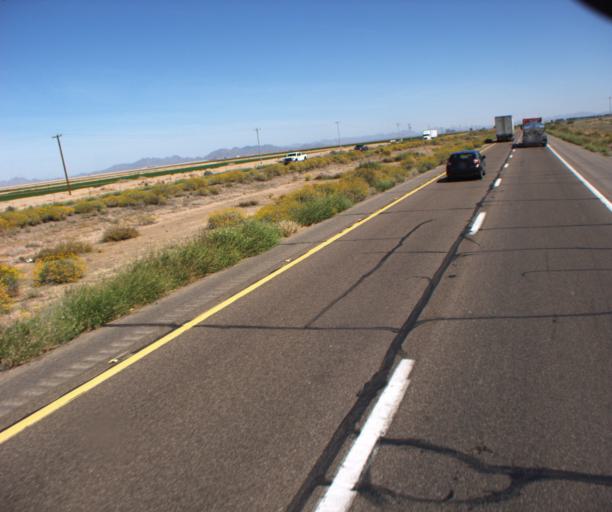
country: US
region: Arizona
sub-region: Maricopa County
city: Gila Bend
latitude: 32.9134
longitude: -112.9431
